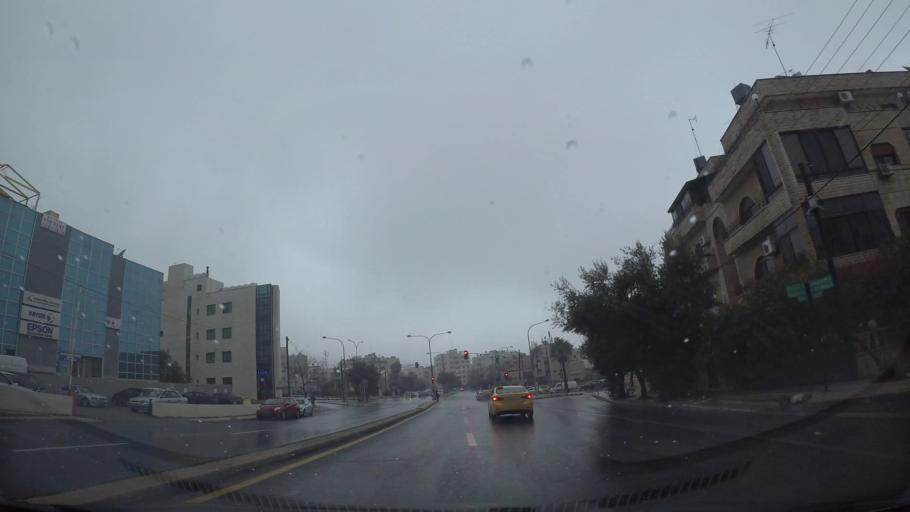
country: JO
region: Amman
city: Al Jubayhah
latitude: 31.9690
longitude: 35.8777
